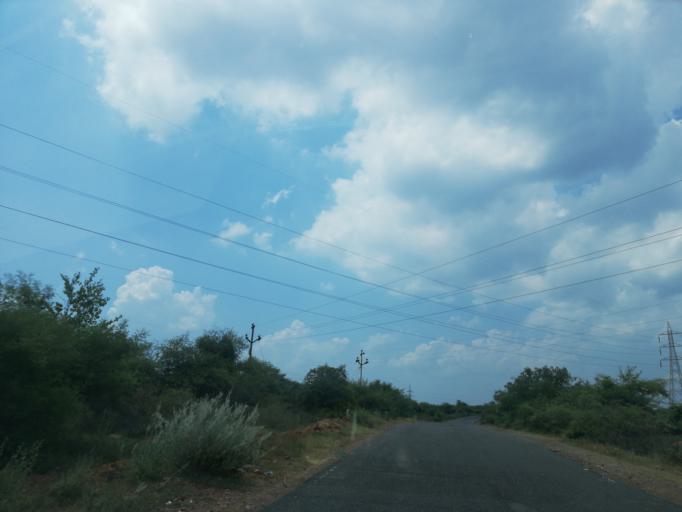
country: IN
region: Andhra Pradesh
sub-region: Guntur
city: Macherla
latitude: 16.5641
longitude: 79.3494
